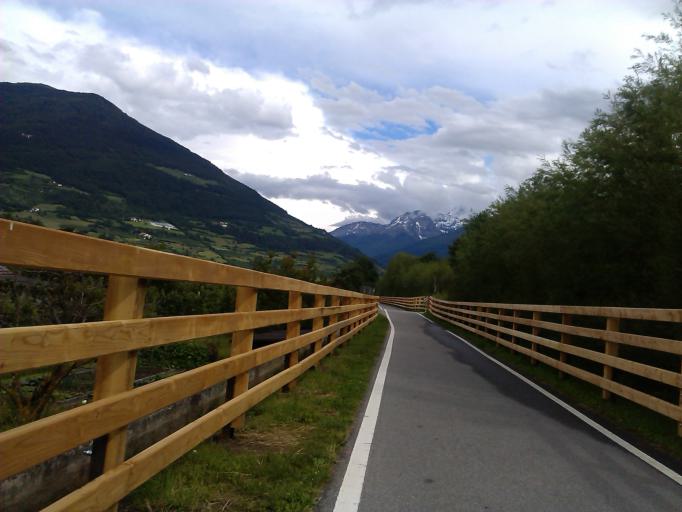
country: IT
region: Trentino-Alto Adige
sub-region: Bolzano
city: Glorenza
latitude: 46.6682
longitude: 10.5563
